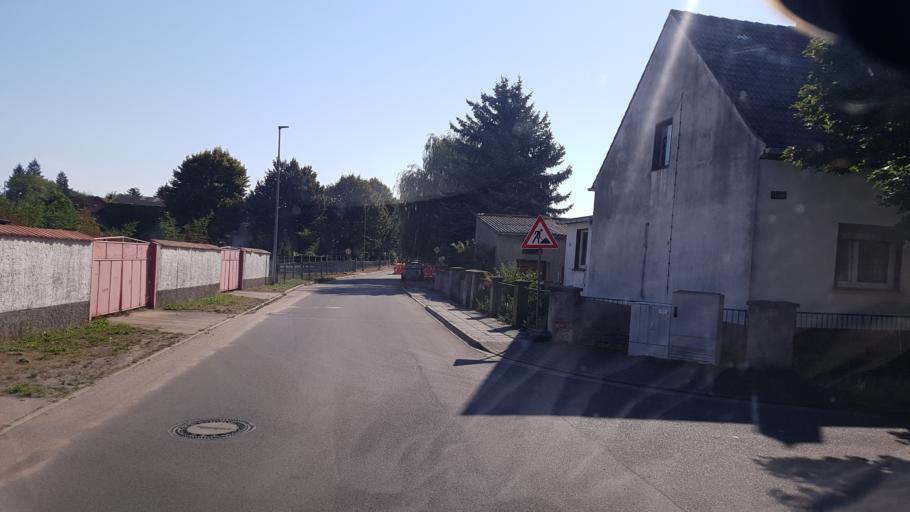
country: DE
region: Brandenburg
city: Plessa
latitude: 51.4700
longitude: 13.6147
